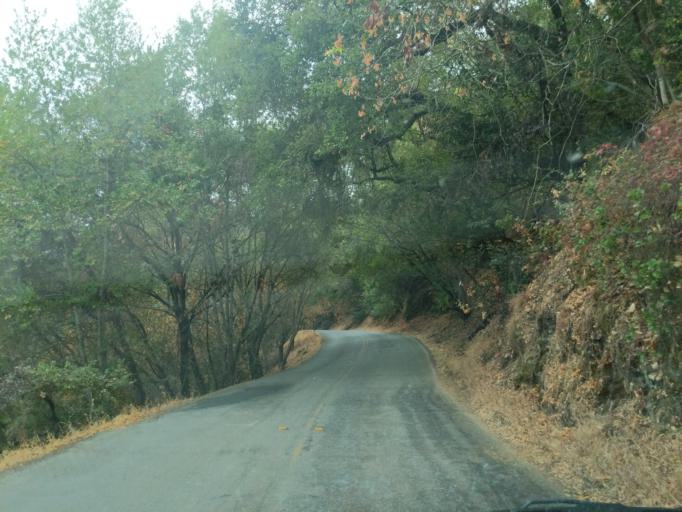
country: US
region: California
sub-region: Santa Clara County
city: Morgan Hill
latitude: 37.1521
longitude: -121.5879
